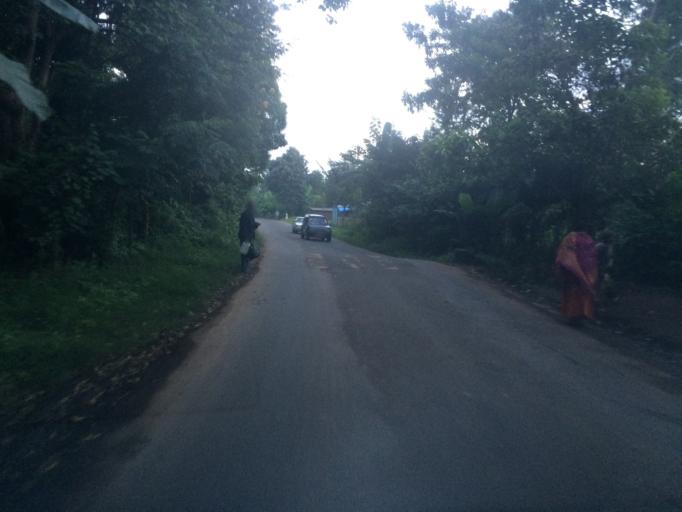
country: TZ
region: Arusha
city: Usa River
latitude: -3.3677
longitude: 36.8165
